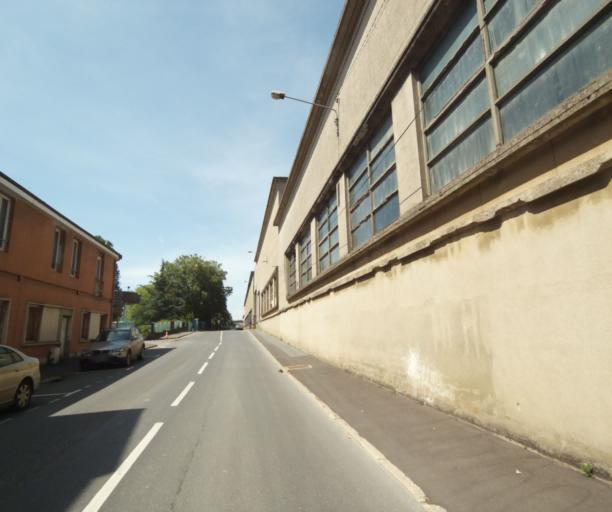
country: FR
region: Champagne-Ardenne
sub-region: Departement des Ardennes
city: Charleville-Mezieres
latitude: 49.7669
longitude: 4.7135
